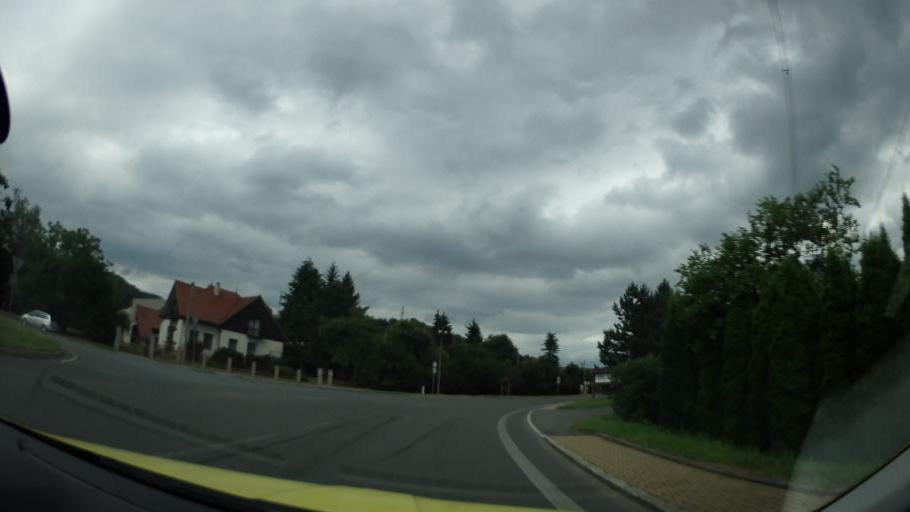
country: CZ
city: Morkov
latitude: 49.5449
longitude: 18.0613
